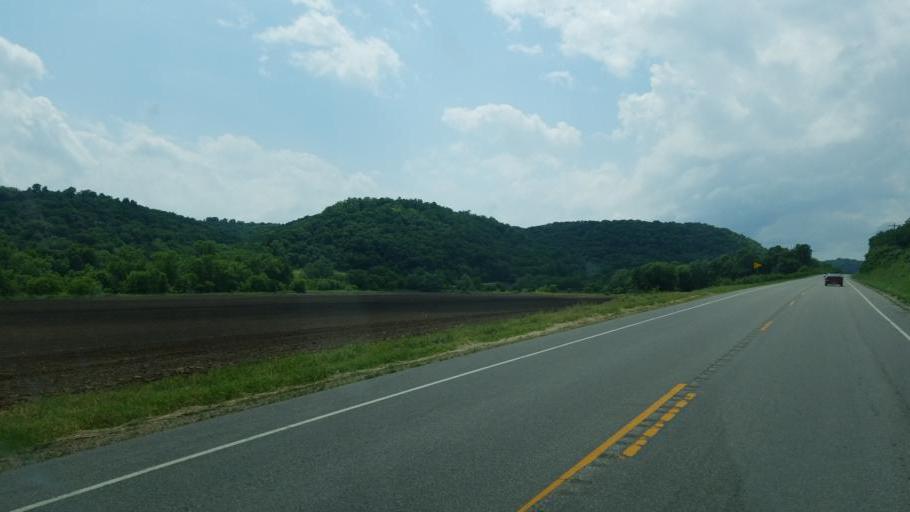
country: US
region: Wisconsin
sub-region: Vernon County
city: Viroqua
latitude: 43.4664
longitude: -90.7183
